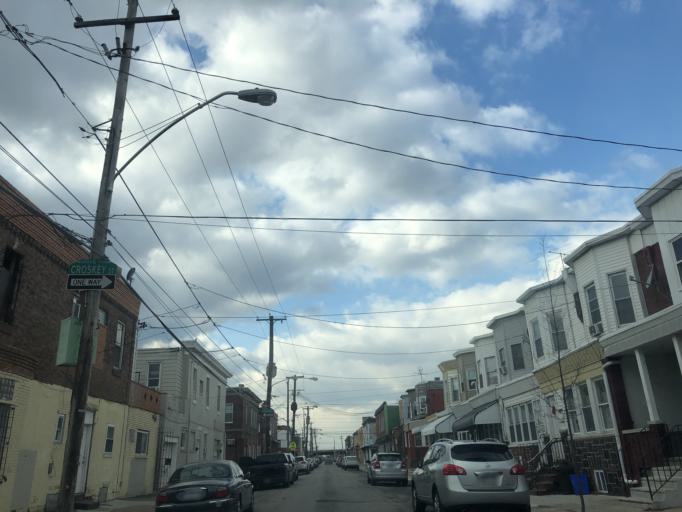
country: US
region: Pennsylvania
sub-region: Philadelphia County
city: Philadelphia
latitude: 39.9274
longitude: -75.1829
